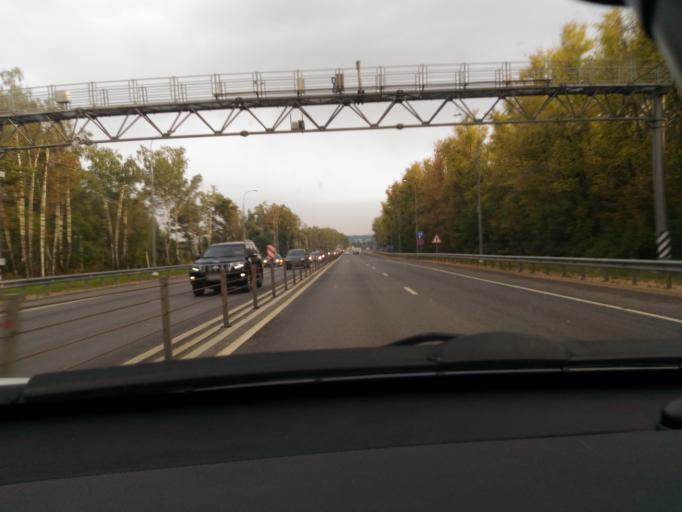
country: RU
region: Moskovskaya
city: Lugovaya
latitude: 56.0619
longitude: 37.5225
